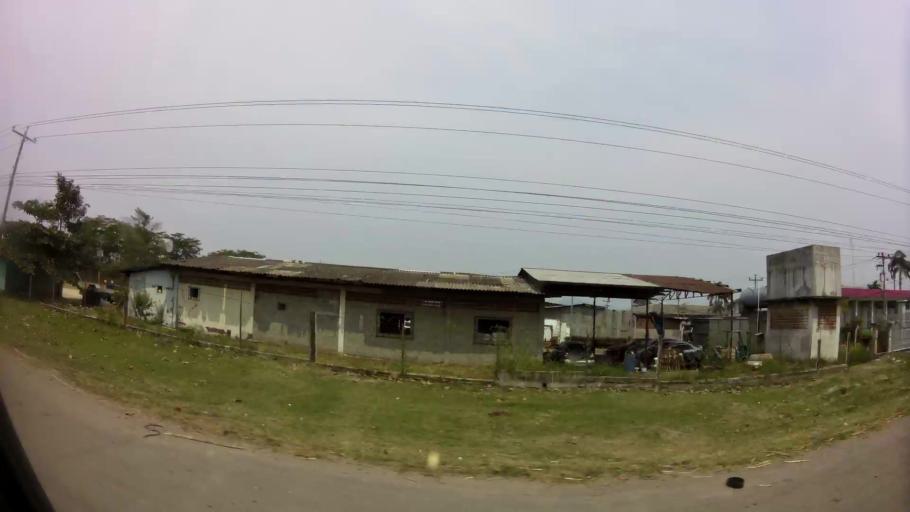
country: HN
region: Cortes
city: Nuevo Chamelecon
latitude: 15.3614
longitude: -87.9856
